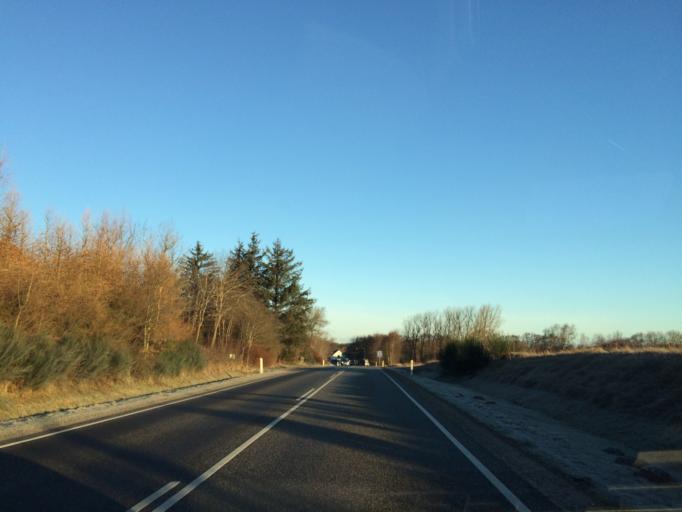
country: DK
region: Central Jutland
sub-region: Holstebro Kommune
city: Ulfborg
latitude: 56.4048
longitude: 8.3148
